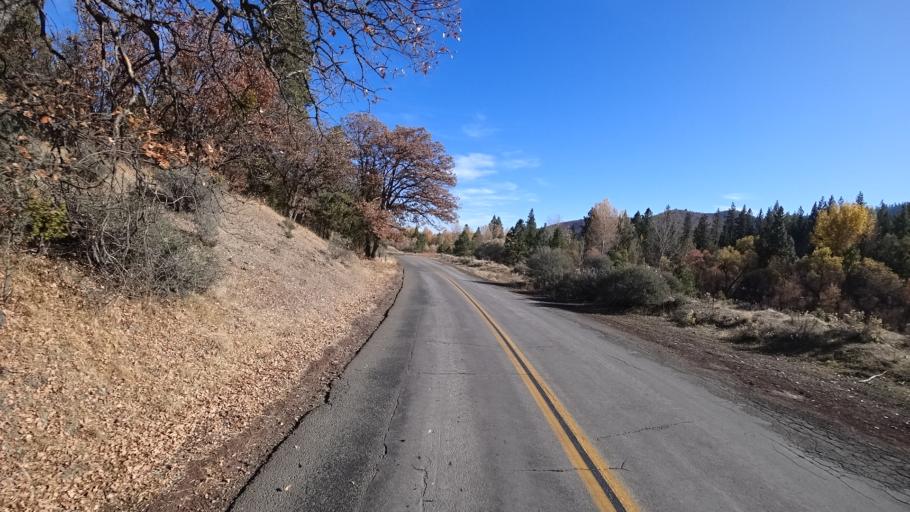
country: US
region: California
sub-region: Siskiyou County
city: Yreka
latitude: 41.7179
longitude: -122.6764
